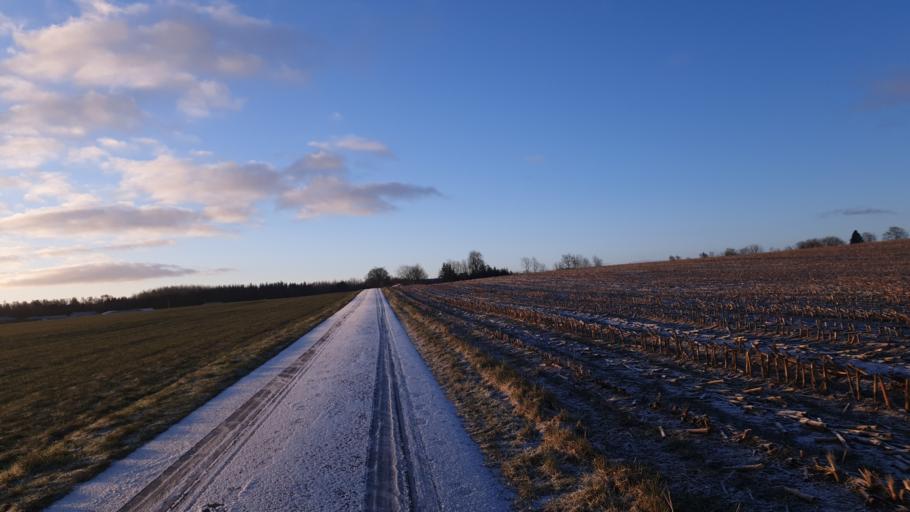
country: DK
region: Central Jutland
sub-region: Hedensted Kommune
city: Hedensted
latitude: 55.8171
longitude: 9.7002
